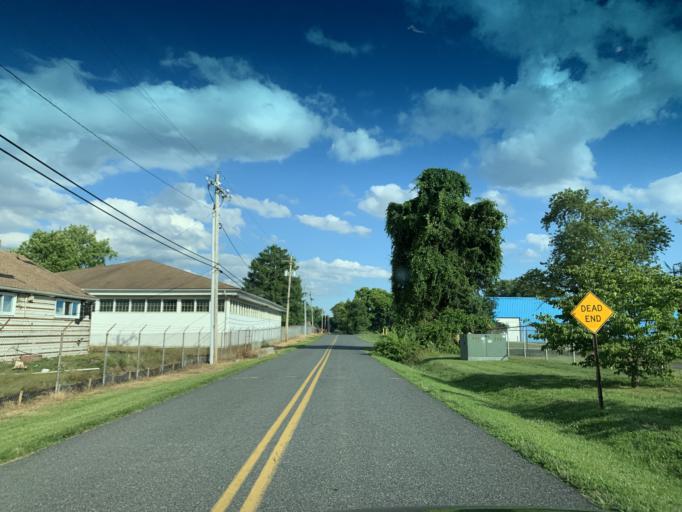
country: US
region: Maryland
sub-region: Harford County
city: Havre de Grace
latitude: 39.5315
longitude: -76.1050
